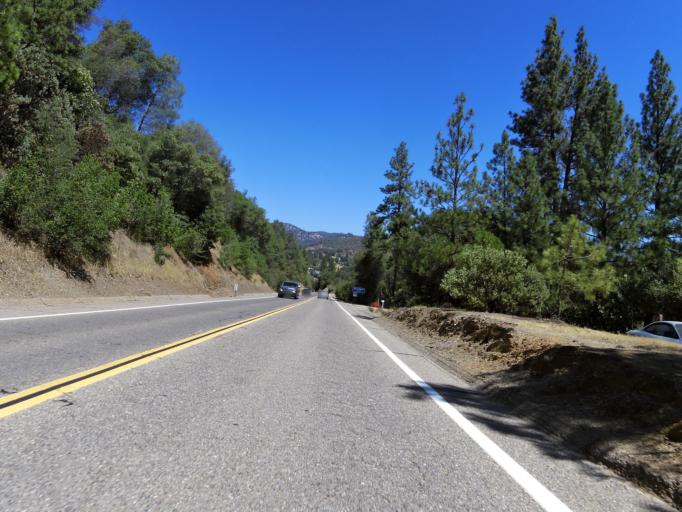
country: US
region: California
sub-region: Mariposa County
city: Mariposa
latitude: 37.4763
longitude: -119.9602
